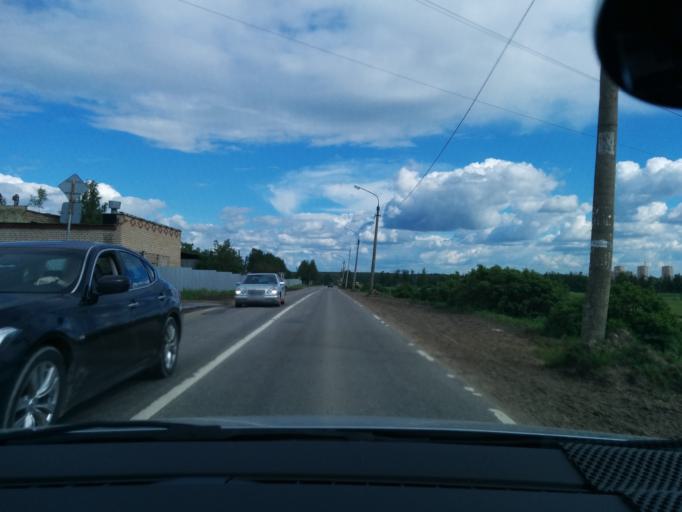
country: RU
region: Moskovskaya
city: Lugovaya
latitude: 56.0445
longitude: 37.4740
